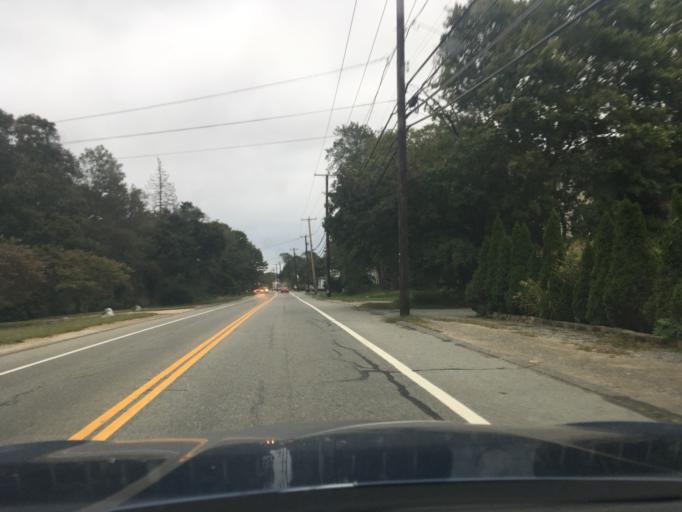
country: US
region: Rhode Island
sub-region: Washington County
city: North Kingstown
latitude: 41.5673
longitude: -71.4685
